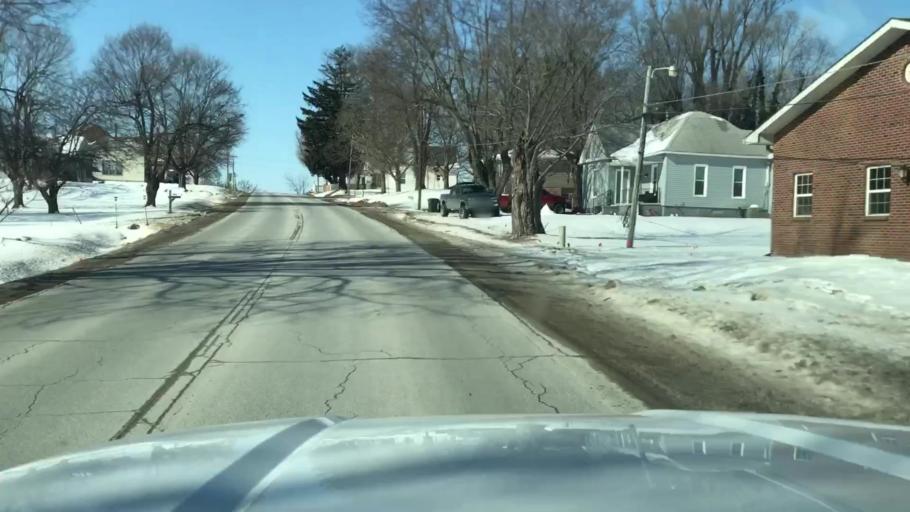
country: US
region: Missouri
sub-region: Andrew County
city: Savannah
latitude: 39.9470
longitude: -94.8342
